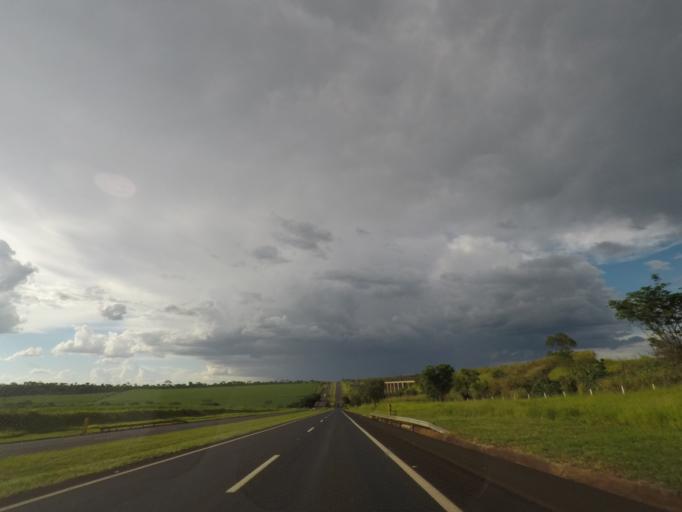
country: BR
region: Sao Paulo
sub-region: Jardinopolis
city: Jardinopolis
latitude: -21.0130
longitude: -47.8439
